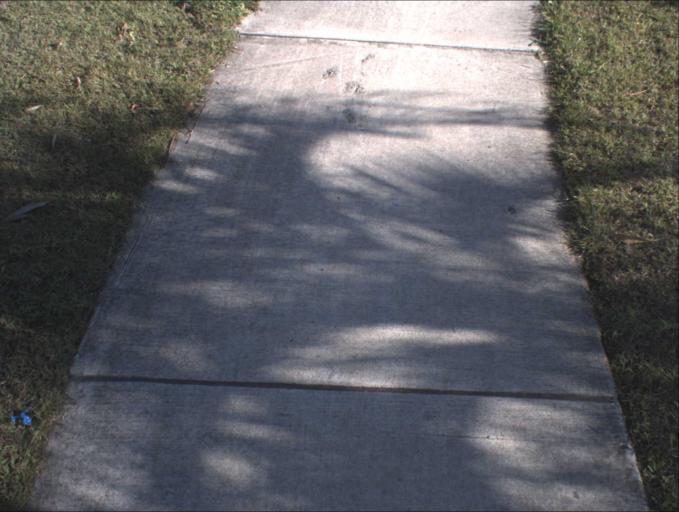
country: AU
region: Queensland
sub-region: Logan
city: Logan Reserve
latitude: -27.6976
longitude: 153.0905
